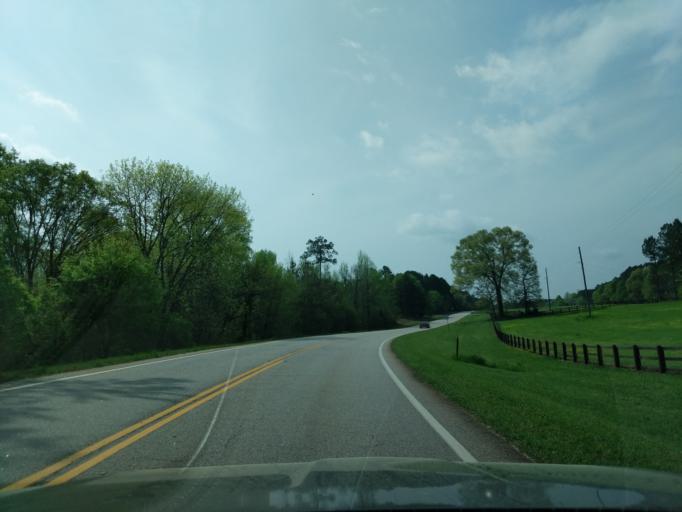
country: US
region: Georgia
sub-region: Lincoln County
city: Lincolnton
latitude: 33.7898
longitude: -82.3801
